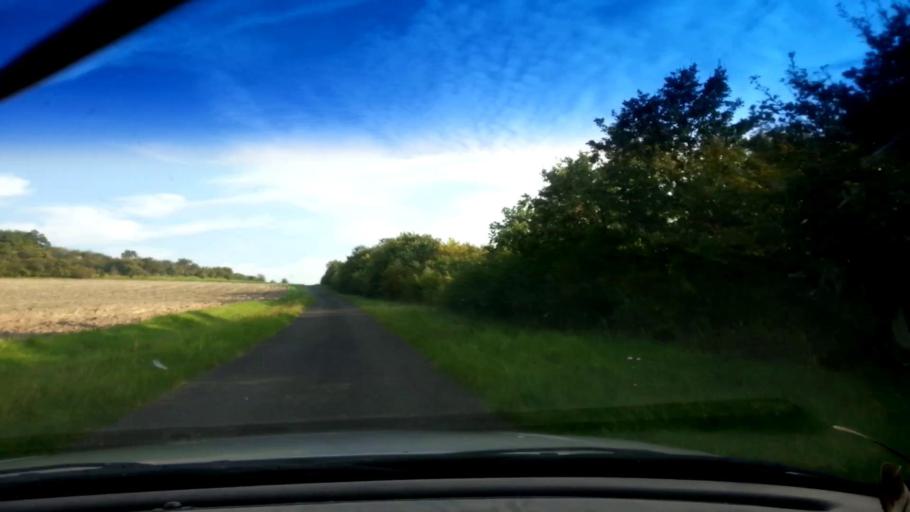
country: DE
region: Bavaria
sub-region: Upper Franconia
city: Lauter
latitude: 49.9475
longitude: 10.7599
